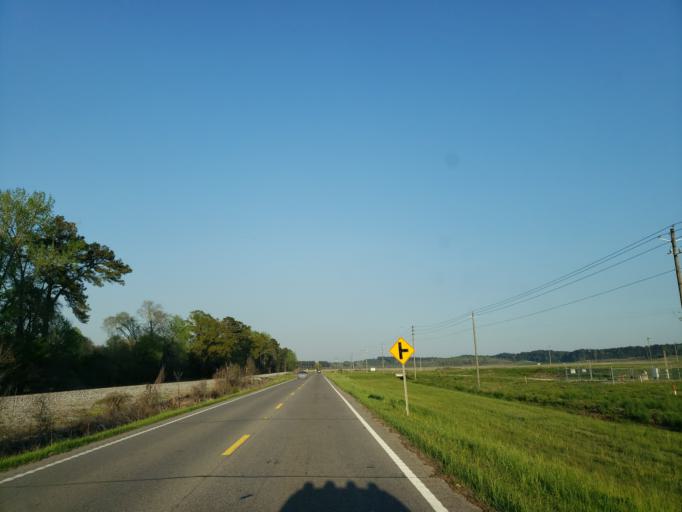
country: US
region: Mississippi
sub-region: Lauderdale County
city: Marion
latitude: 32.3941
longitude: -88.6338
